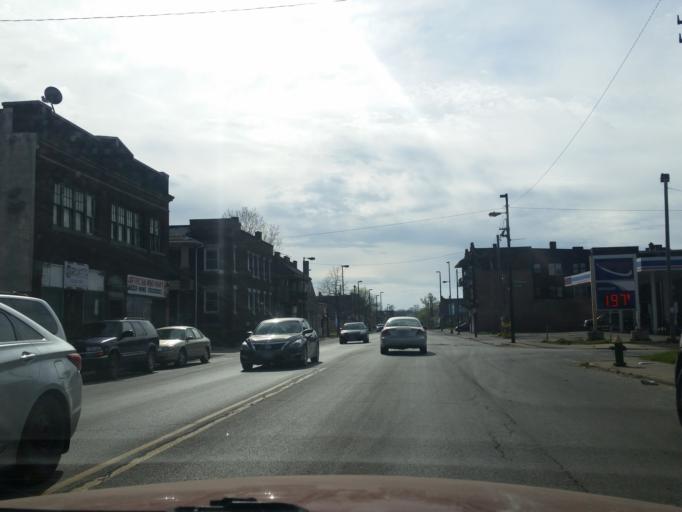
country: US
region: Ohio
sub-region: Cuyahoga County
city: East Cleveland
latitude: 41.5231
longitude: -81.5966
